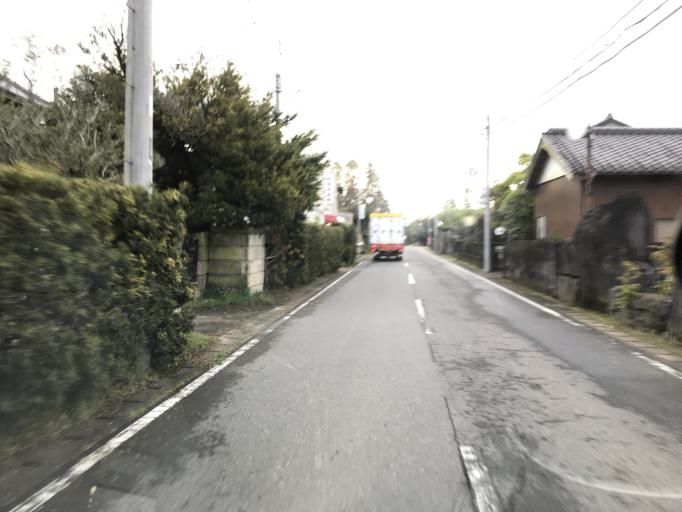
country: JP
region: Chiba
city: Yokaichiba
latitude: 35.7485
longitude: 140.5538
